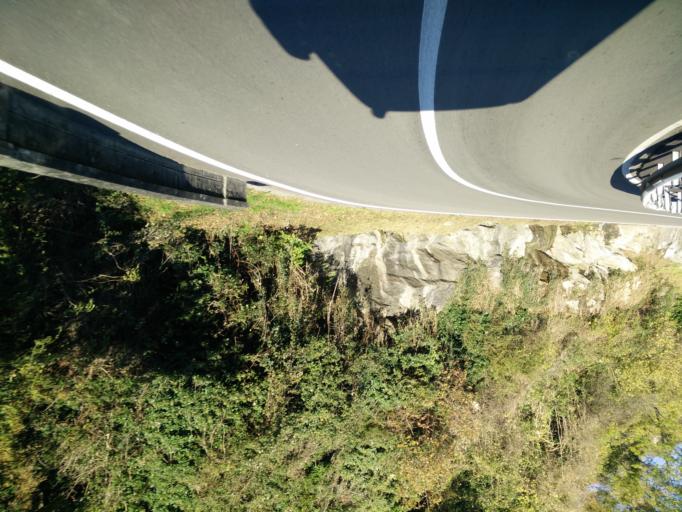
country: IT
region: Trentino-Alto Adige
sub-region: Bolzano
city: San Leonardo in Passiria
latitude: 46.8217
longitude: 11.2207
